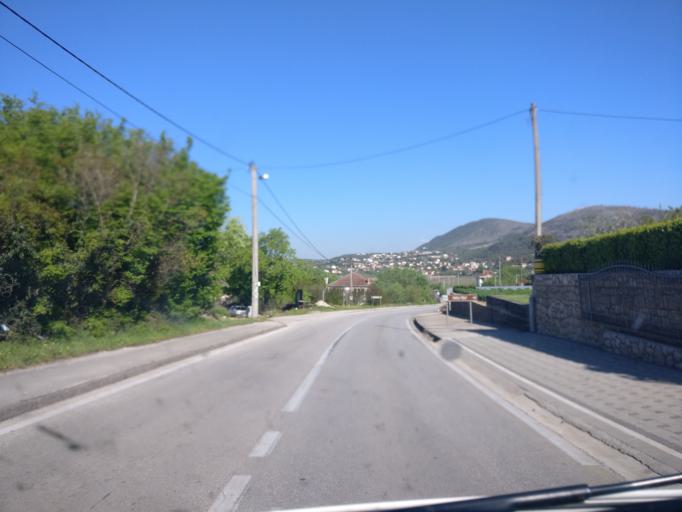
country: BA
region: Federation of Bosnia and Herzegovina
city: Capljina
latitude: 43.1285
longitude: 17.6777
